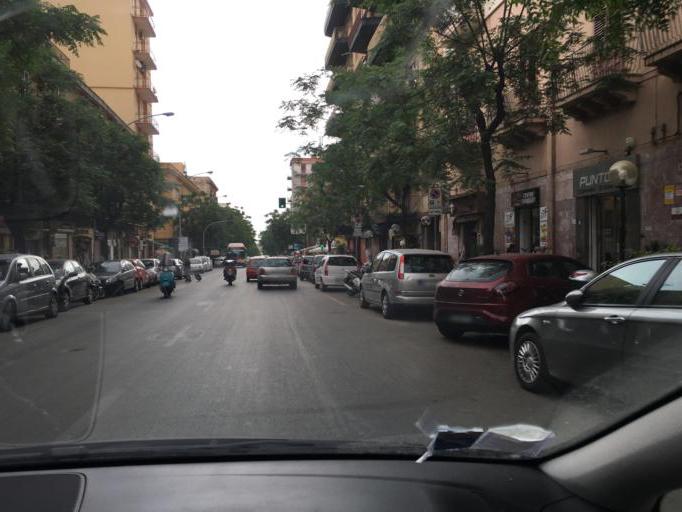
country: IT
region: Sicily
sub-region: Palermo
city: Palermo
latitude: 38.1069
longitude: 13.3398
